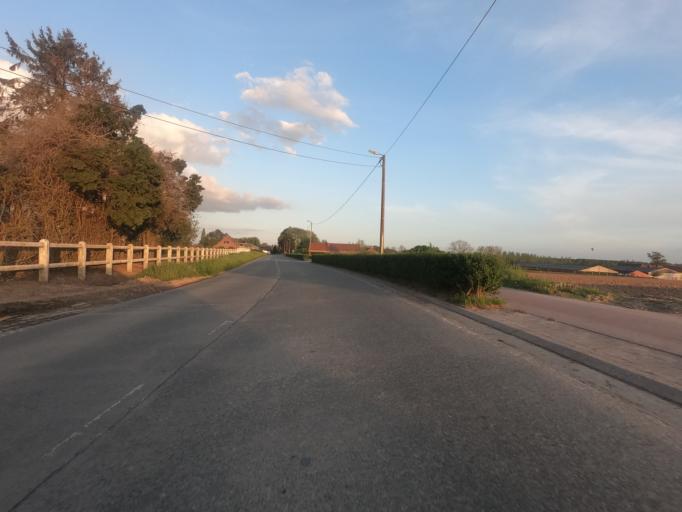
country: BE
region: Flanders
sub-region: Provincie Vlaams-Brabant
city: Pepingen
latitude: 50.7834
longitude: 4.1605
